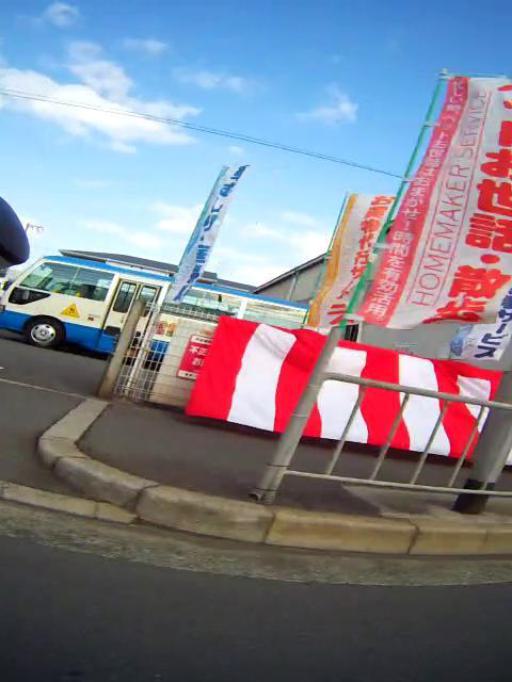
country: JP
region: Osaka
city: Daitocho
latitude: 34.6878
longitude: 135.6221
